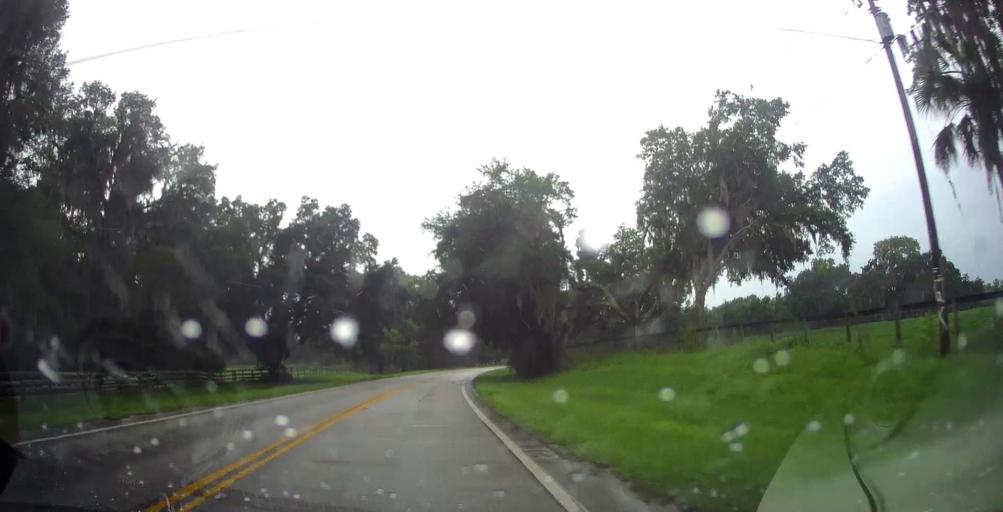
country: US
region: Florida
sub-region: Marion County
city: Citra
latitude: 29.3994
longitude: -82.2477
